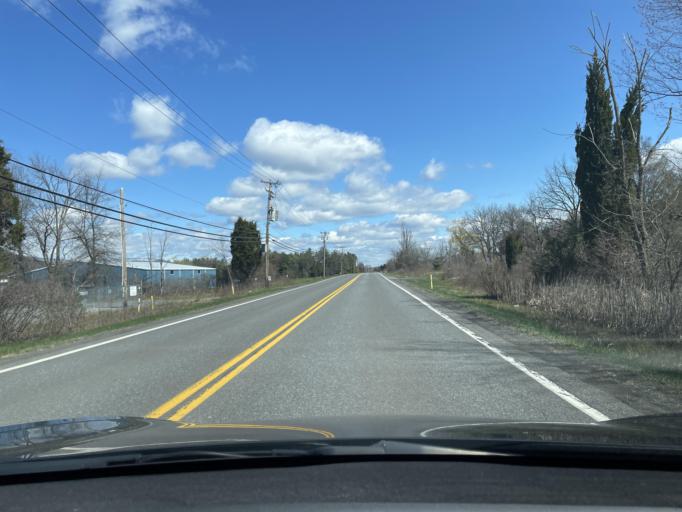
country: US
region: New York
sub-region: Ulster County
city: Glasco
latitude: 42.0445
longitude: -73.9807
